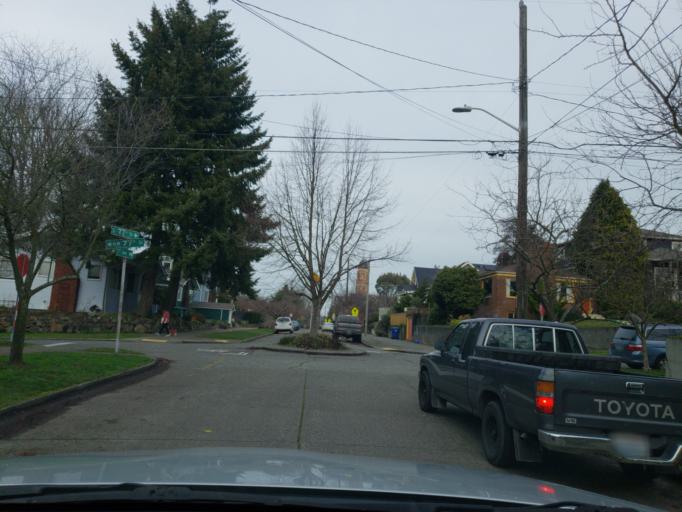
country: US
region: Washington
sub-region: King County
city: Shoreline
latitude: 47.6845
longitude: -122.3580
